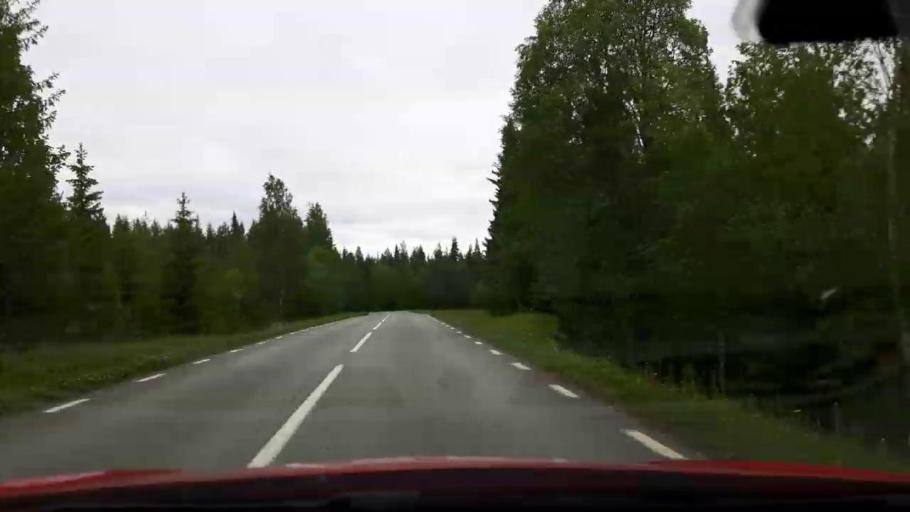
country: SE
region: Jaemtland
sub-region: Stroemsunds Kommun
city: Stroemsund
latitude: 63.4806
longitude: 15.4443
